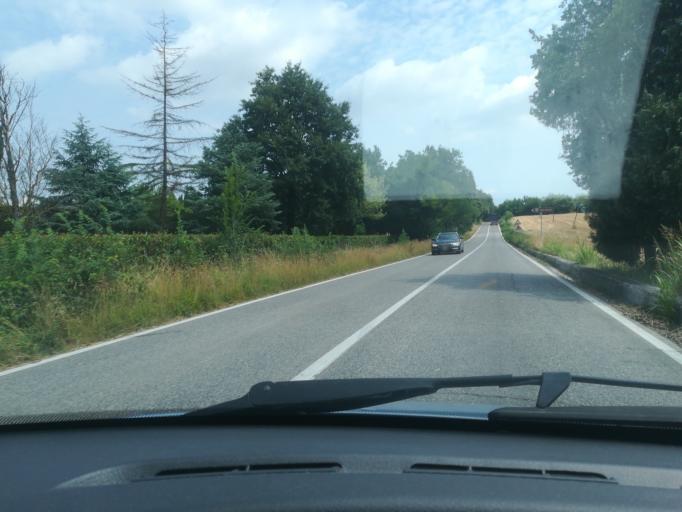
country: IT
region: The Marches
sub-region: Provincia di Macerata
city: Recanati
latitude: 43.3669
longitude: 13.5138
